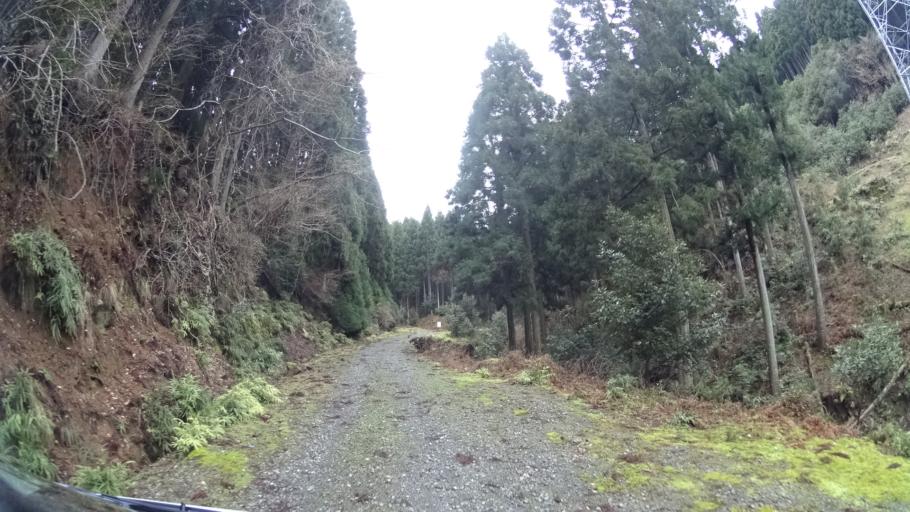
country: JP
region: Kyoto
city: Ayabe
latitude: 35.3102
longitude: 135.3765
